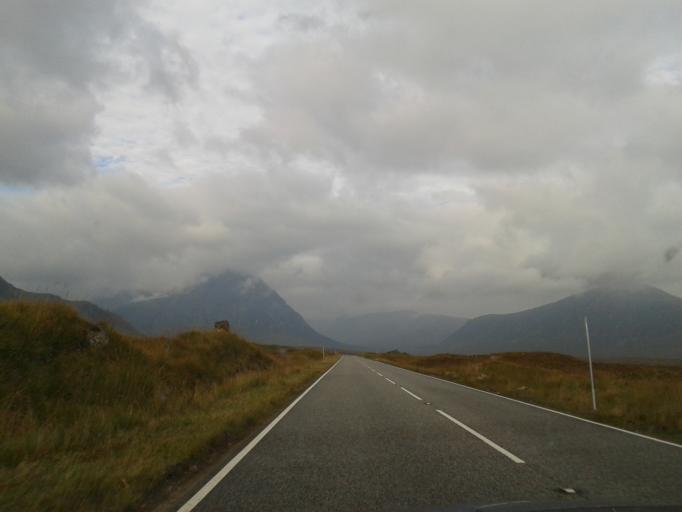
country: GB
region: Scotland
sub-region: Highland
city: Spean Bridge
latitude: 56.6343
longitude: -4.7993
